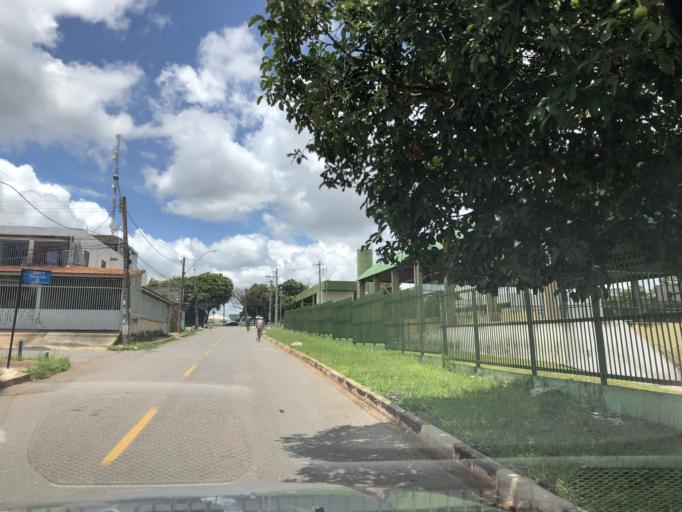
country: BR
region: Federal District
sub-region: Brasilia
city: Brasilia
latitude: -15.8010
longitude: -48.1251
